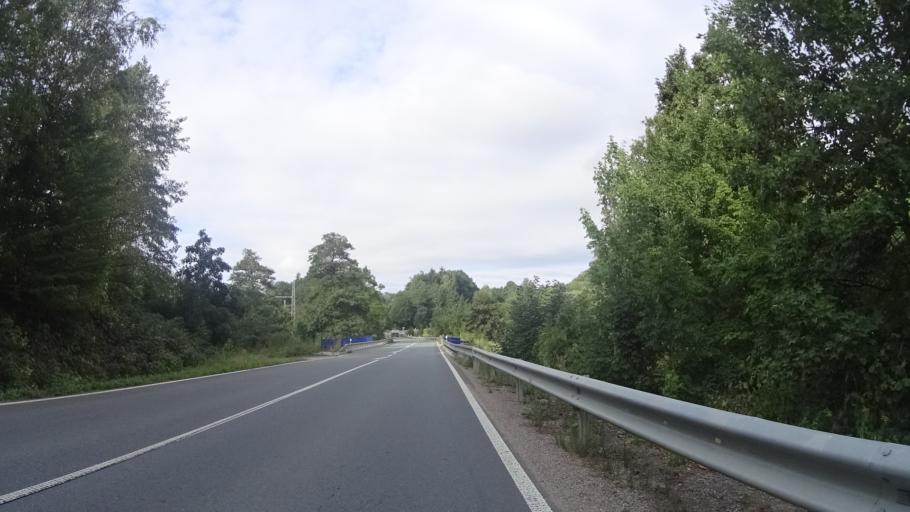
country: CZ
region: Olomoucky
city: Stity
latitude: 49.8631
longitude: 16.7185
